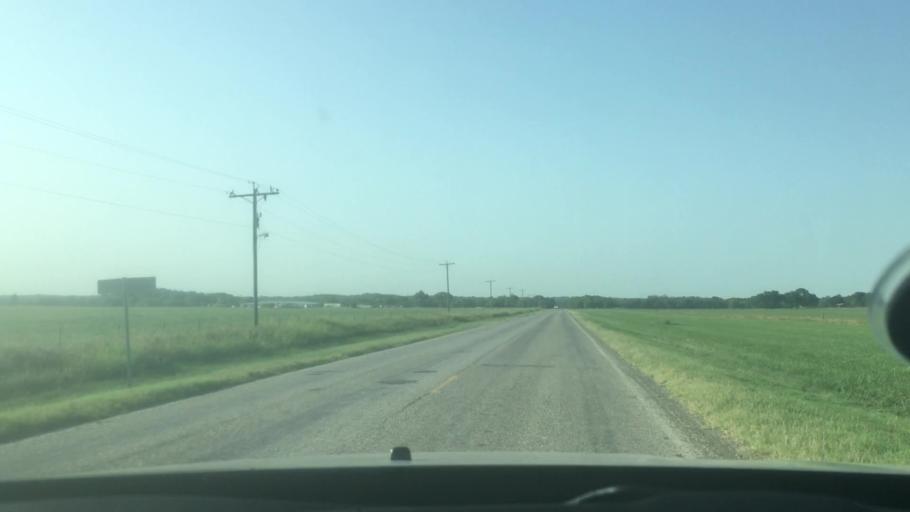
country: US
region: Oklahoma
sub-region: Johnston County
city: Tishomingo
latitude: 34.3450
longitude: -96.4228
